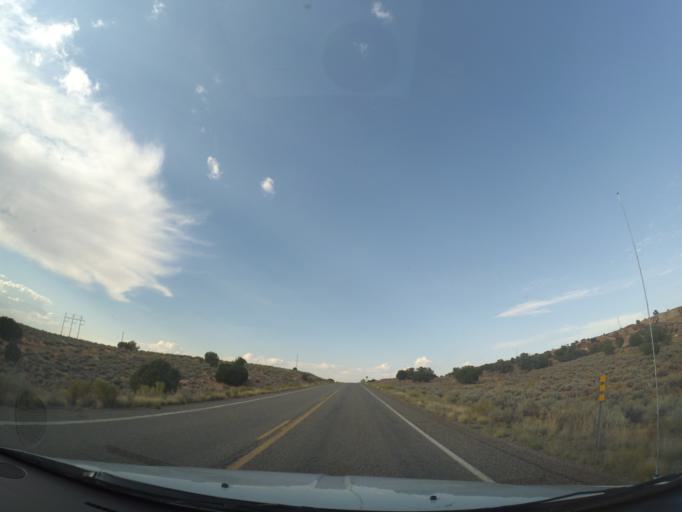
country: US
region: Arizona
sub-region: Coconino County
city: LeChee
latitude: 36.7084
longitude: -111.4427
